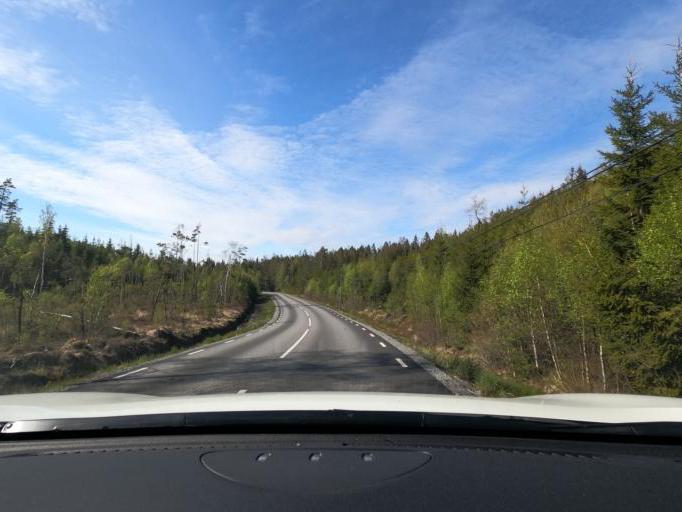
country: SE
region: Vaestra Goetaland
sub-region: Harryda Kommun
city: Landvetter
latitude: 57.6326
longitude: 12.2654
